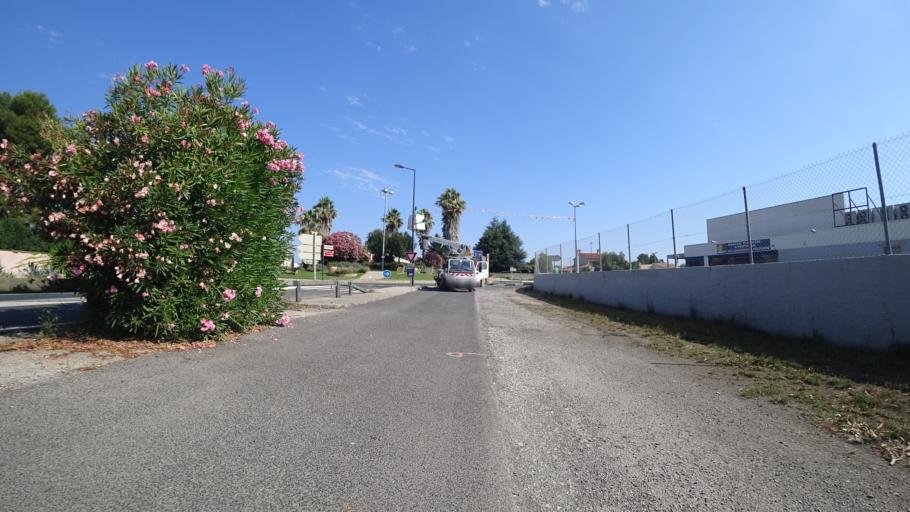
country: FR
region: Languedoc-Roussillon
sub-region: Departement des Pyrenees-Orientales
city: Bompas
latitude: 42.7300
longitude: 2.9250
